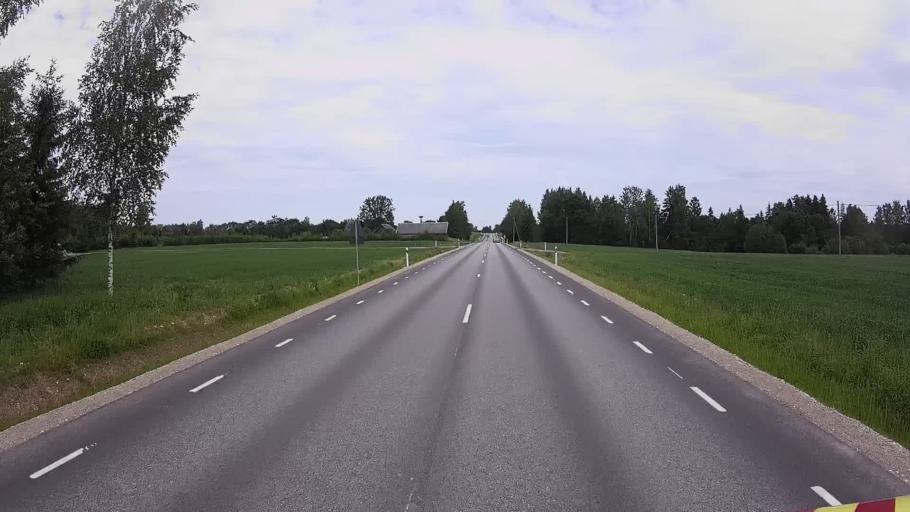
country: EE
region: Viljandimaa
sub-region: Viljandi linn
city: Viljandi
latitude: 58.2604
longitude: 25.5875
